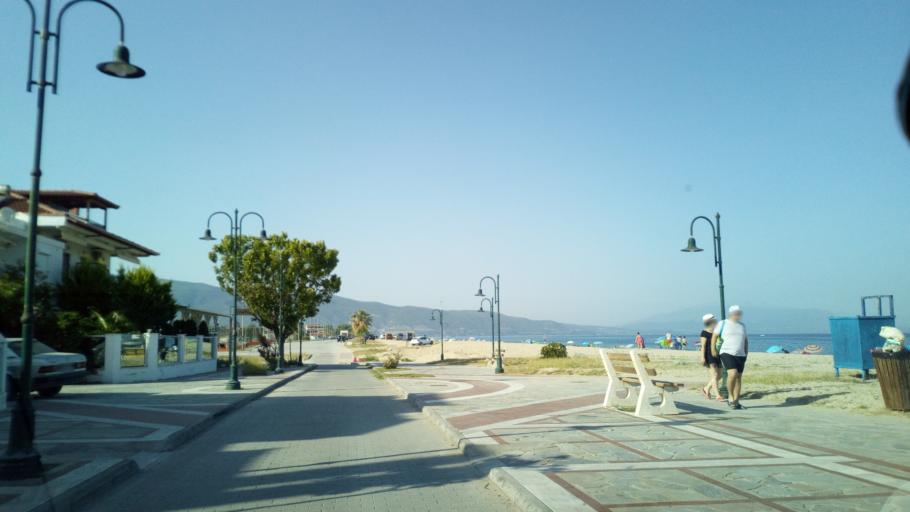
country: GR
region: Central Macedonia
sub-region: Nomos Thessalonikis
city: Nea Vrasna
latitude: 40.7114
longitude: 23.7044
